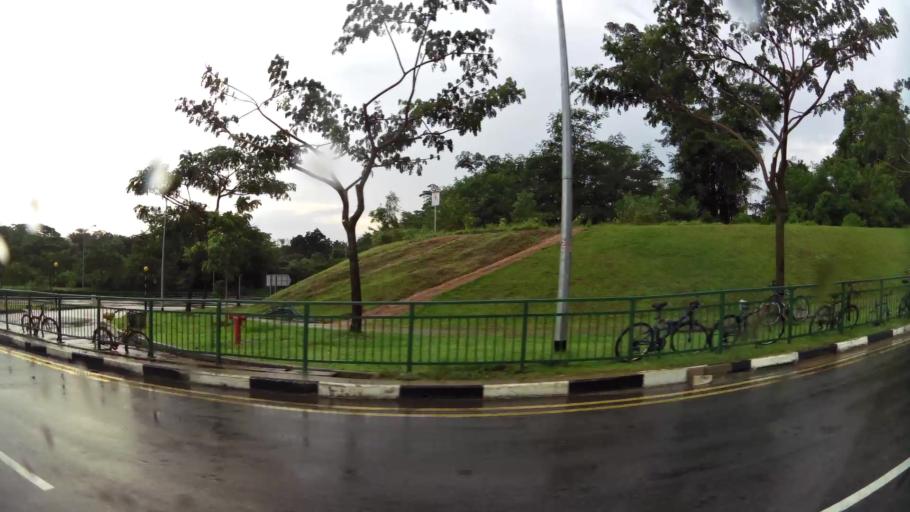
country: MY
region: Johor
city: Kampung Pasir Gudang Baru
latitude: 1.3959
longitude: 103.8689
